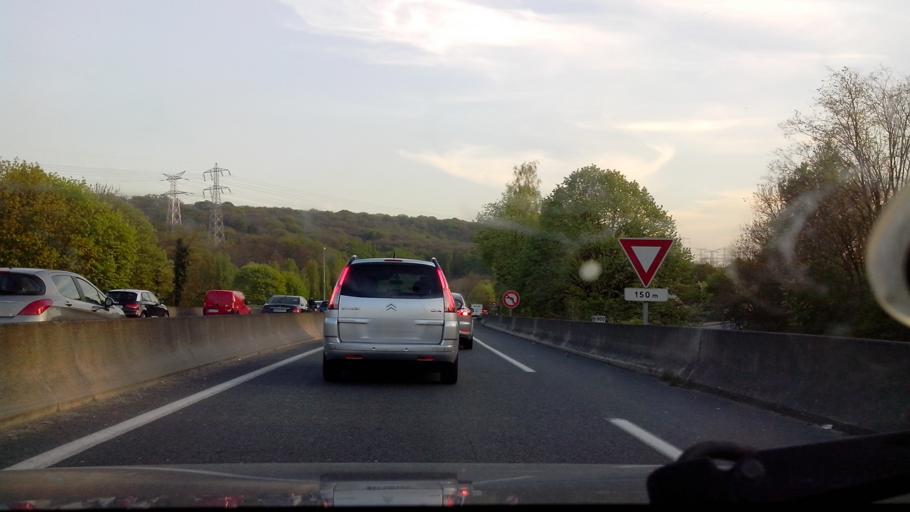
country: FR
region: Ile-de-France
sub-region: Departement de l'Essonne
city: Bievres
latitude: 48.7676
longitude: 2.2299
